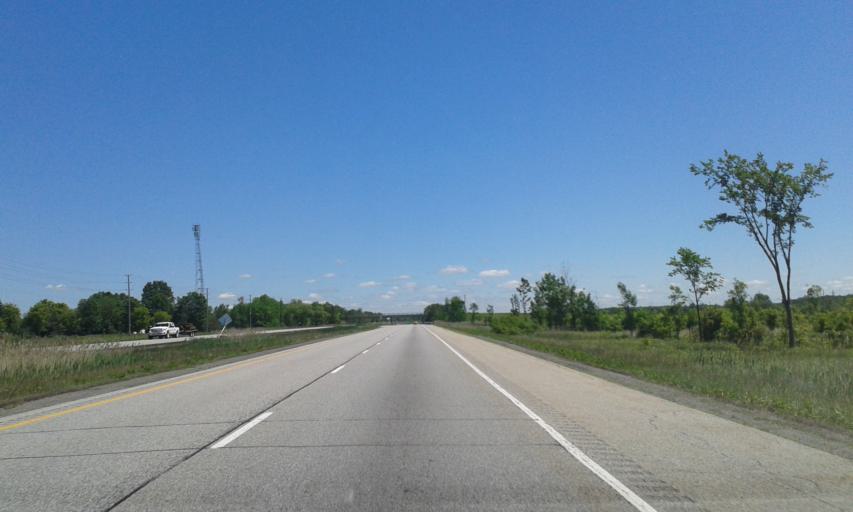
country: US
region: New York
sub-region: St. Lawrence County
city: Norfolk
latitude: 44.8896
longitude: -75.2655
